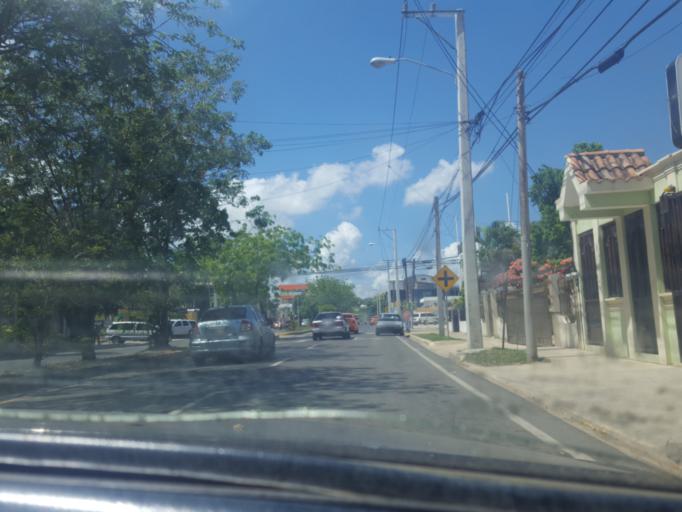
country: DO
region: Santiago
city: Santiago de los Caballeros
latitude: 19.4929
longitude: -70.7032
